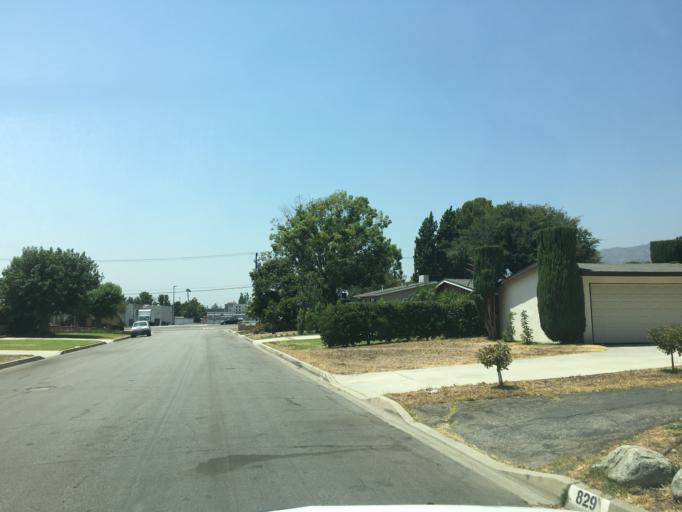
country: US
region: California
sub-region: Los Angeles County
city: Glendora
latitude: 34.1300
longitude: -117.8801
